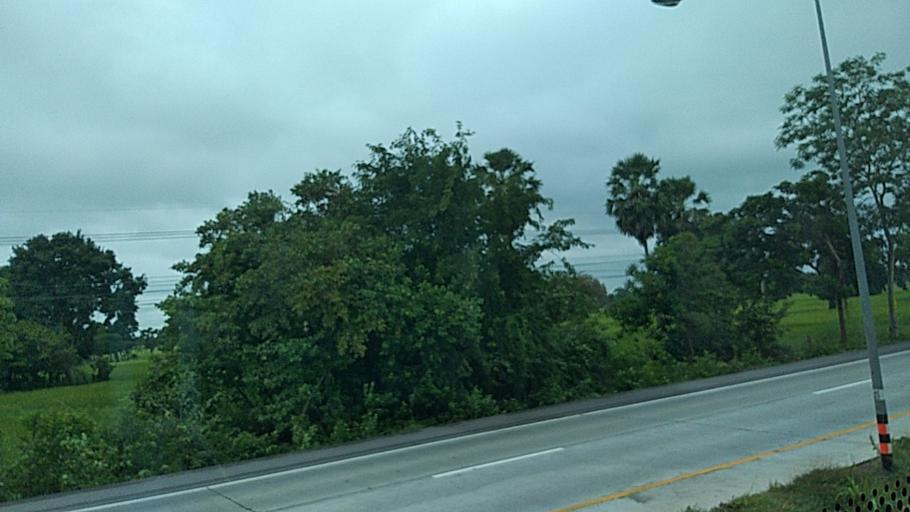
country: TH
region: Nakhon Ratchasima
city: Bua Lai
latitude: 15.6294
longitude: 102.5677
